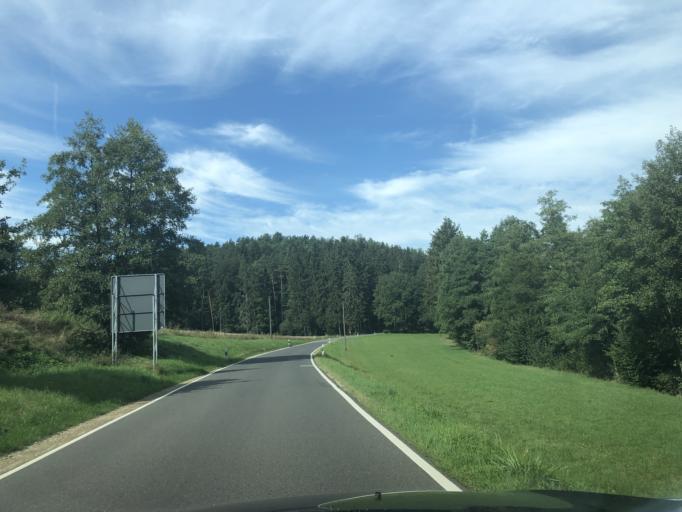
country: DE
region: Bavaria
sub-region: Upper Palatinate
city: Pressath
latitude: 49.7775
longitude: 11.9154
